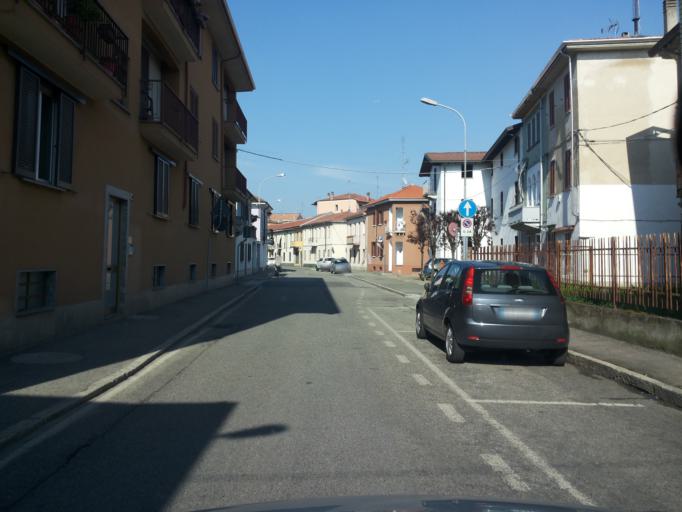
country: IT
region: Lombardy
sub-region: Provincia di Pavia
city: Cilavegna
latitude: 45.3085
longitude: 8.7410
